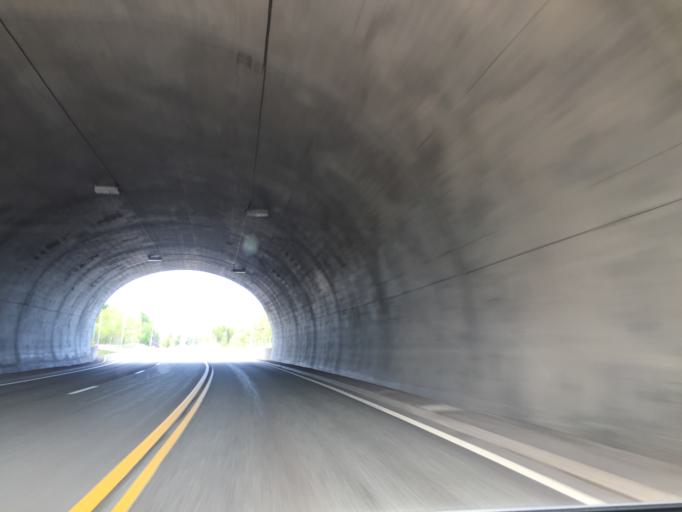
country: NO
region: Vestfold
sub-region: Holmestrand
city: Gullhaug
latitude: 59.5072
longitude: 10.1990
